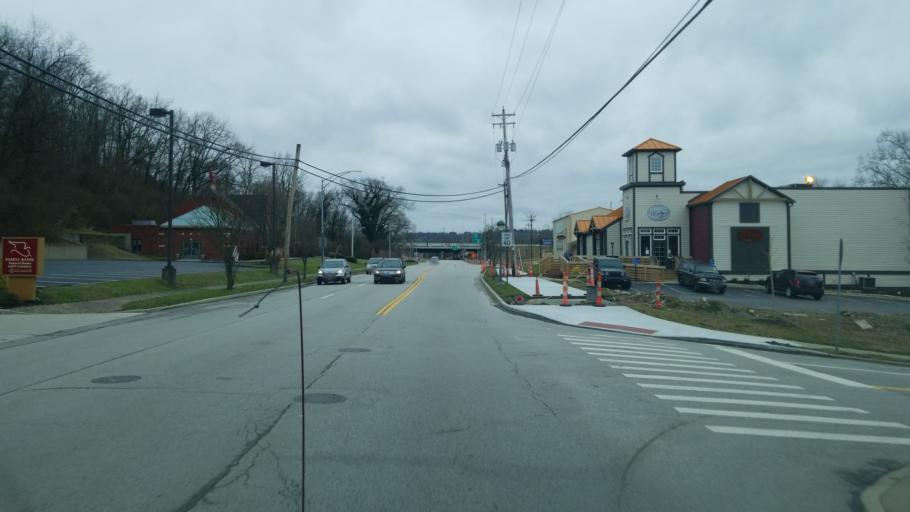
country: US
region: Kentucky
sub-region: Campbell County
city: Fort Thomas
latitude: 39.0644
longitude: -84.4232
